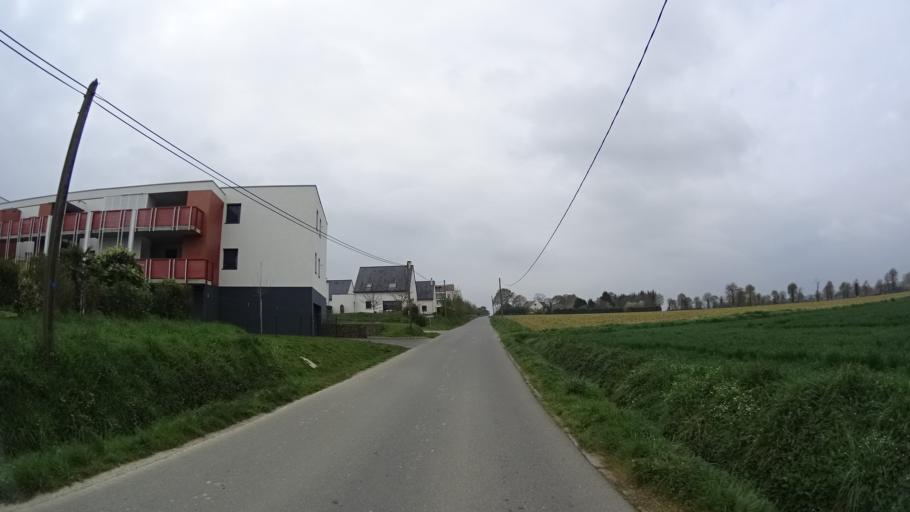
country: FR
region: Brittany
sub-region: Departement d'Ille-et-Vilaine
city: Saint-Gilles
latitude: 48.1494
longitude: -1.8425
